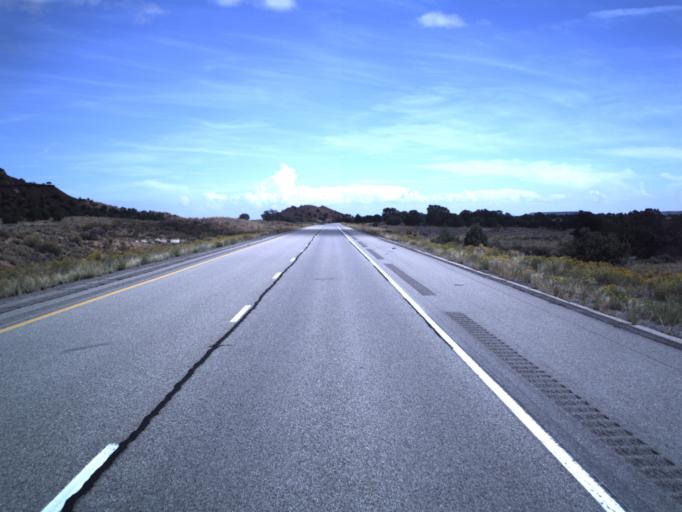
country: US
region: Utah
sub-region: Emery County
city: Castle Dale
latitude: 38.8692
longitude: -110.7220
